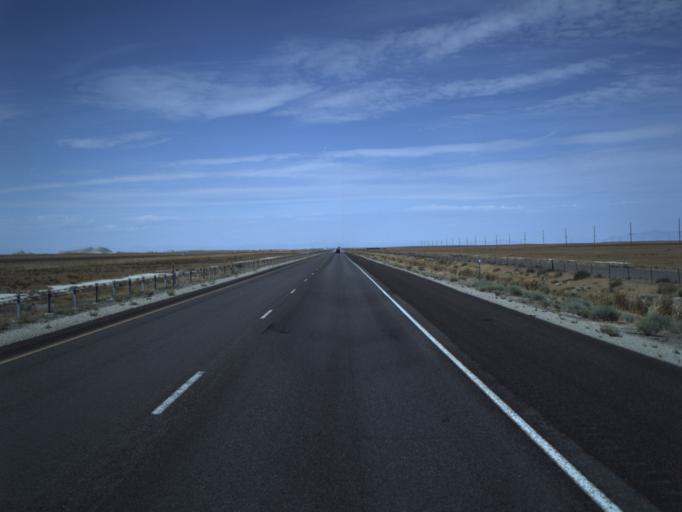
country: US
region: Utah
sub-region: Tooele County
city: Grantsville
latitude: 40.7264
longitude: -113.1753
